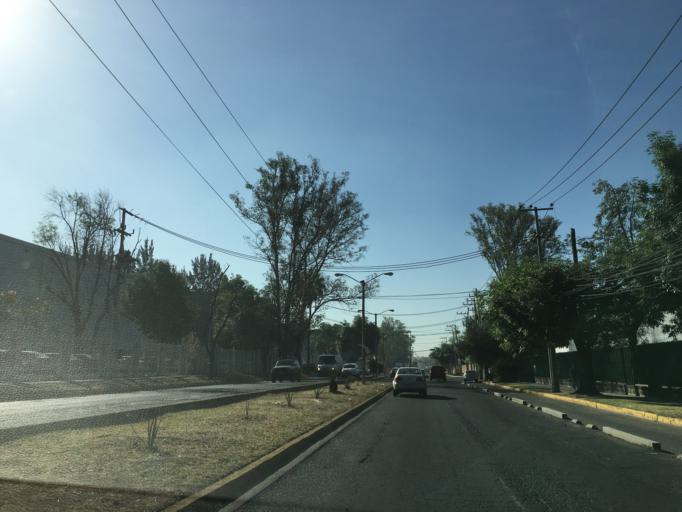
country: MX
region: Jalisco
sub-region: Tlajomulco de Zuniga
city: La Tijera
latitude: 20.6152
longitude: -103.4199
